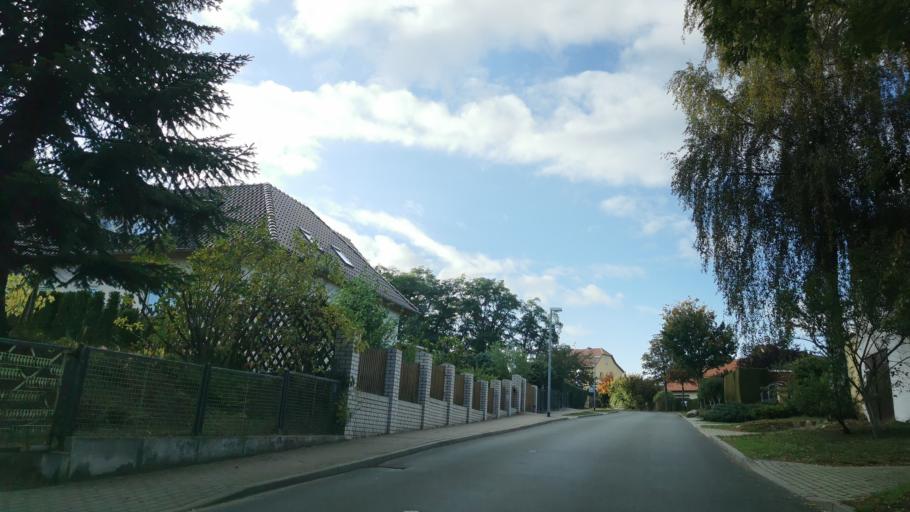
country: DE
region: Brandenburg
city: Werder
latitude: 52.3573
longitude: 12.9057
